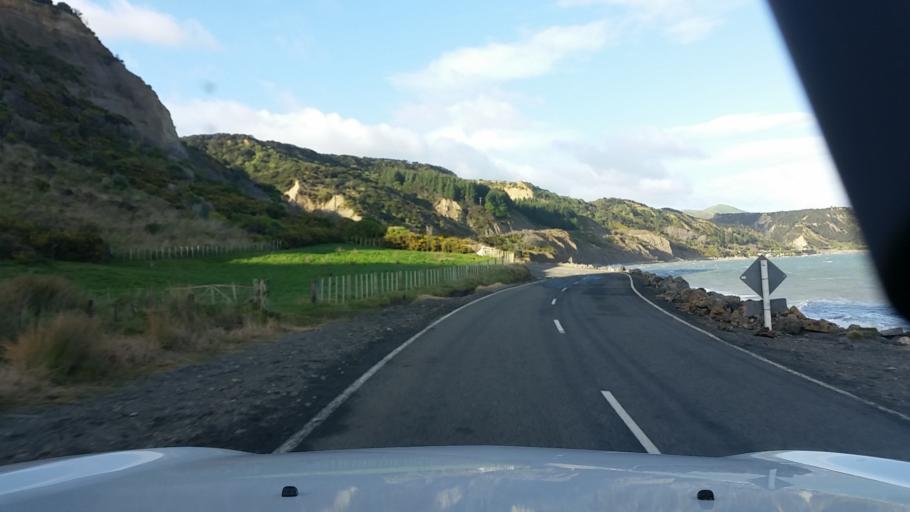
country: NZ
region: Wellington
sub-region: South Wairarapa District
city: Waipawa
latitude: -41.4470
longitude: 175.2198
